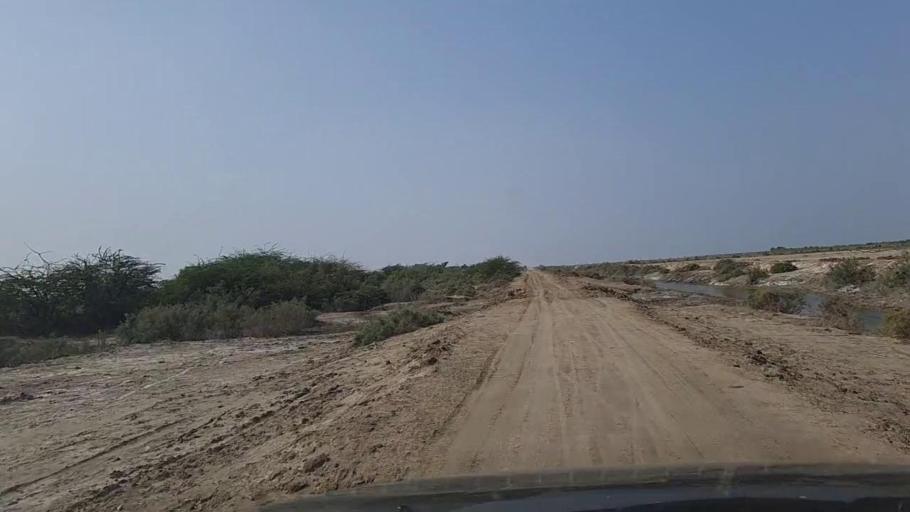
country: PK
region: Sindh
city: Gharo
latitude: 24.7074
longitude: 67.5452
